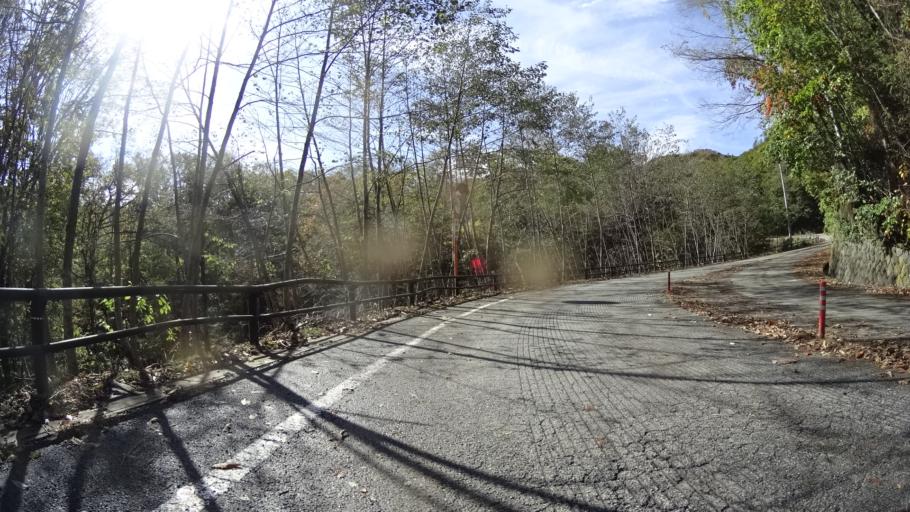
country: JP
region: Yamanashi
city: Enzan
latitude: 35.7886
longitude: 138.8005
